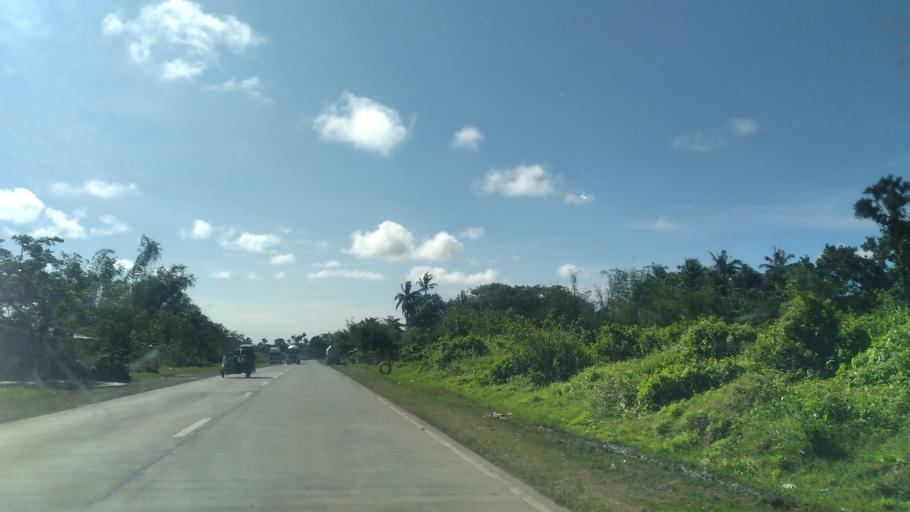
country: PH
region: Calabarzon
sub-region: Province of Quezon
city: Isabang
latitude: 13.9577
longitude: 121.5783
